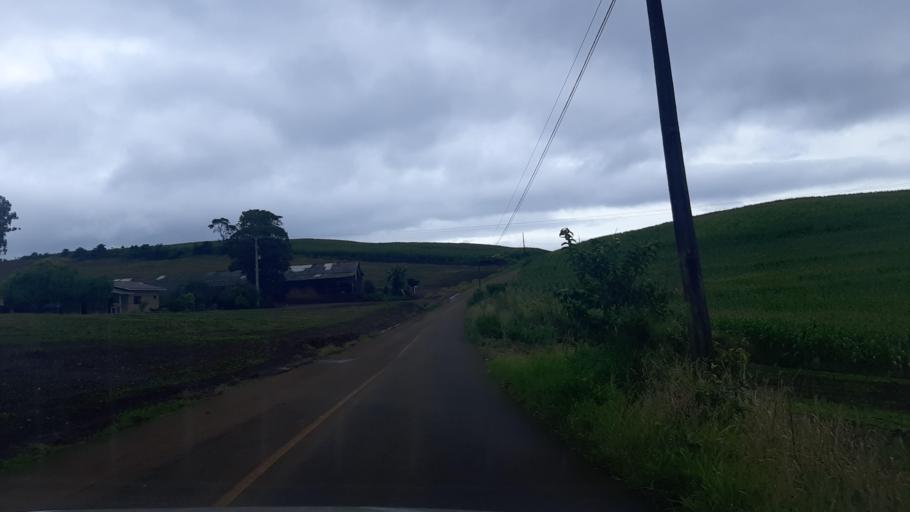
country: BR
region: Parana
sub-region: Ampere
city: Ampere
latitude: -26.0410
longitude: -53.4927
